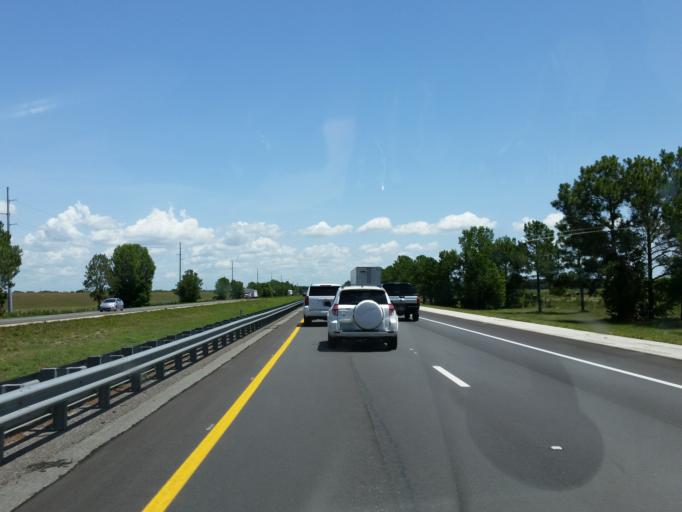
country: US
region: Florida
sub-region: Sumter County
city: Lake Panasoffkee
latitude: 28.7335
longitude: -82.1117
